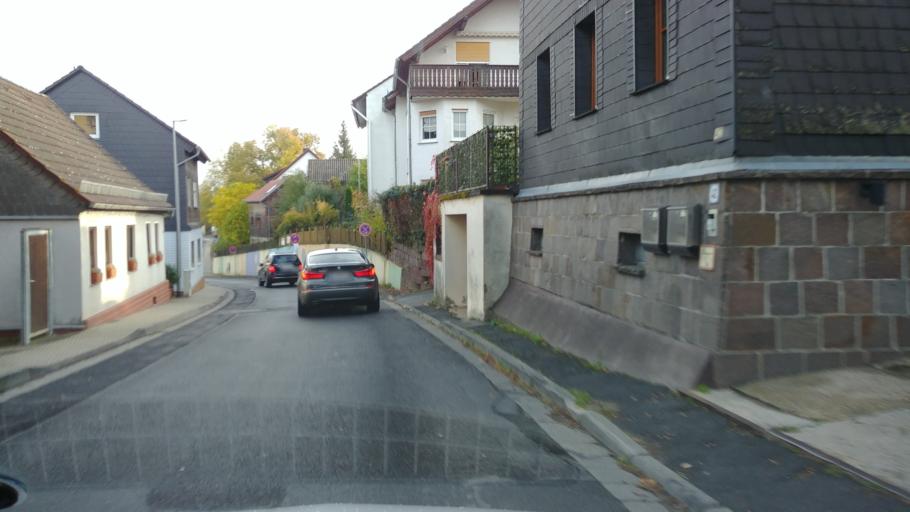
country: DE
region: Hesse
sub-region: Regierungsbezirk Darmstadt
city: Schlangenbad
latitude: 50.1237
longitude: 8.1211
